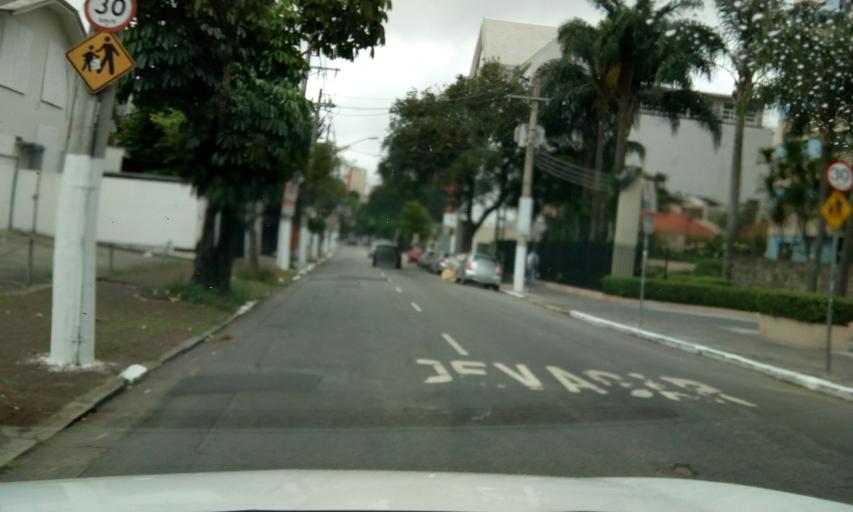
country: BR
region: Sao Paulo
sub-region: Sao Paulo
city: Sao Paulo
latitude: -23.5844
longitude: -46.6380
